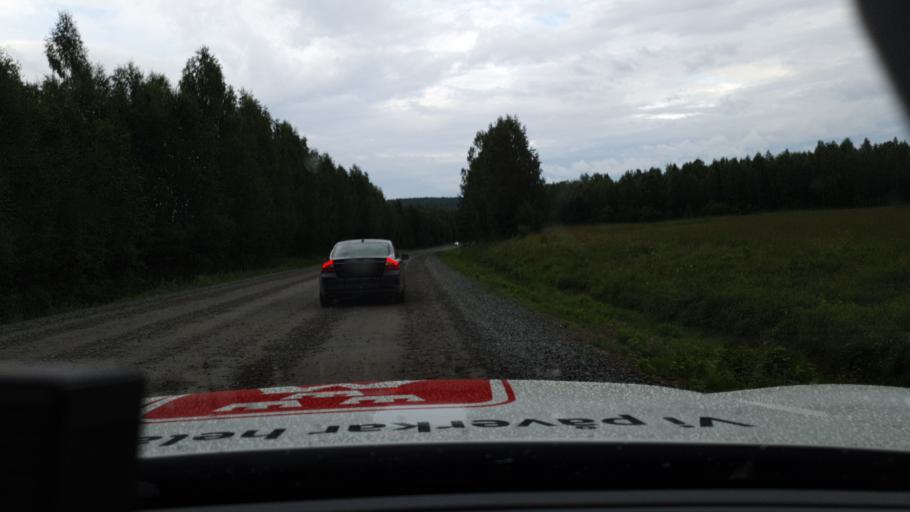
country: SE
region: Norrbotten
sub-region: Bodens Kommun
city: Boden
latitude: 65.8505
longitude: 21.5769
